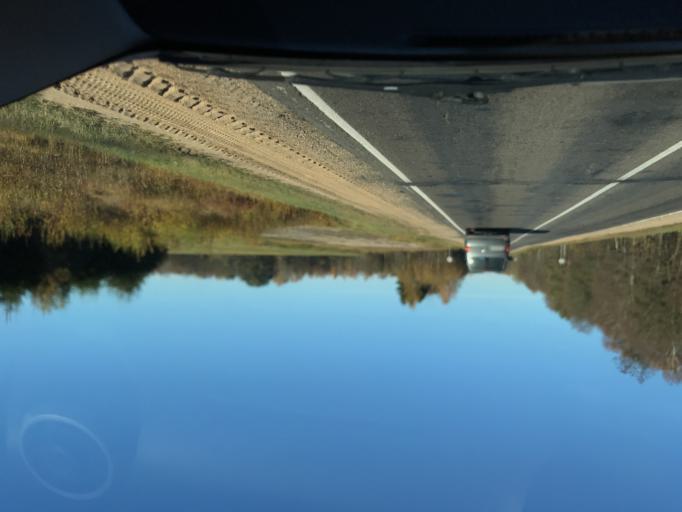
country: BY
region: Vitebsk
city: Polatsk
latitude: 55.3250
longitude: 28.7828
